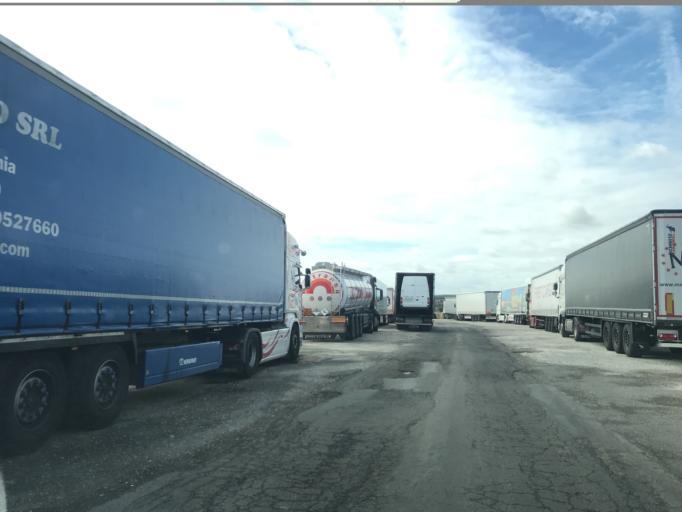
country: FR
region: Poitou-Charentes
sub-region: Departement de la Charente
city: Ruffec
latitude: 45.9844
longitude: 0.2007
